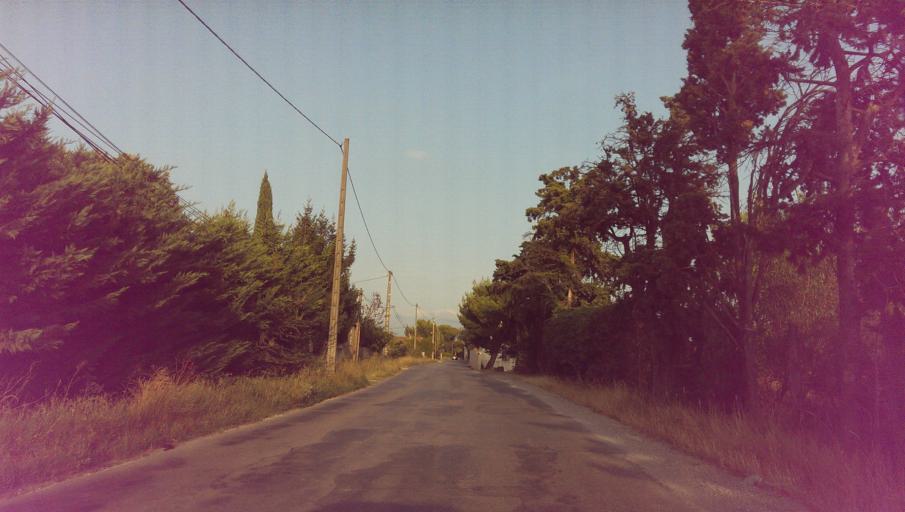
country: FR
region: Provence-Alpes-Cote d'Azur
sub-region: Departement du Vaucluse
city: Carpentras
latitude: 44.0312
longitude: 5.0618
